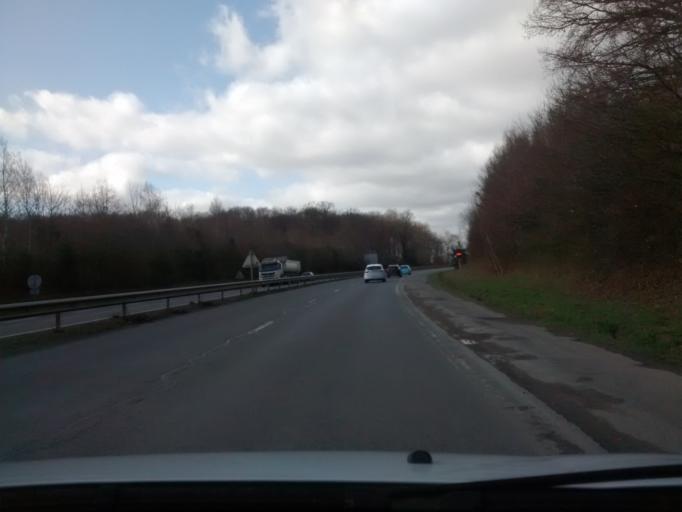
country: FR
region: Brittany
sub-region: Departement d'Ille-et-Vilaine
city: Cesson-Sevigne
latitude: 48.1370
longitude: -1.6253
